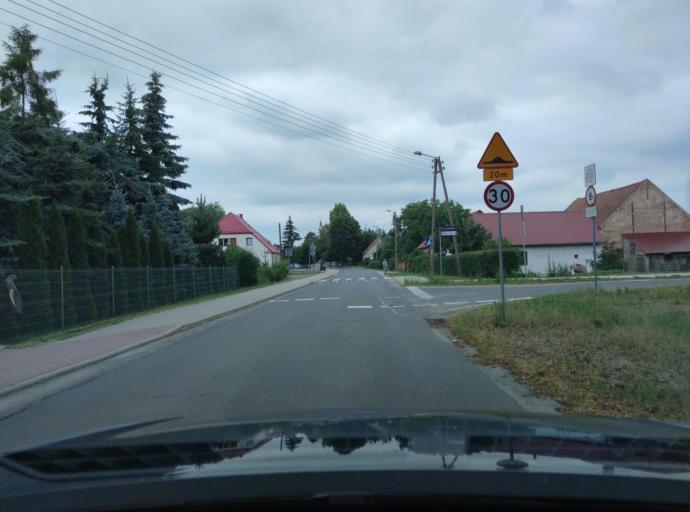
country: PL
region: Lower Silesian Voivodeship
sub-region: Powiat wroclawski
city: Kobierzyce
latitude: 50.9511
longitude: 16.8917
